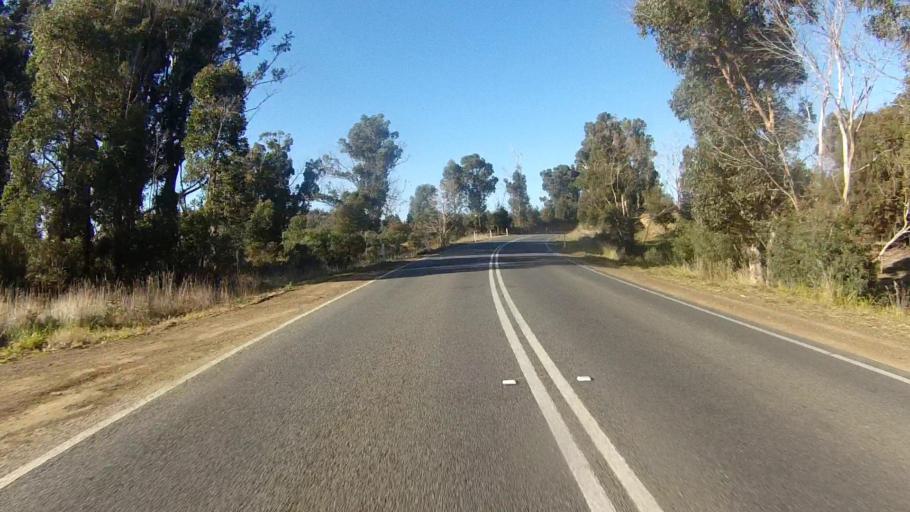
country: AU
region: Tasmania
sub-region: Sorell
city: Sorell
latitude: -42.8383
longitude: 147.8077
